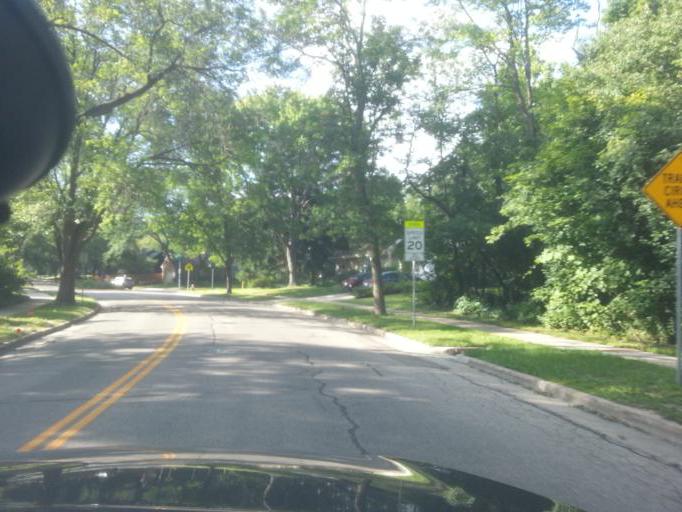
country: US
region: Wisconsin
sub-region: Dane County
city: Middleton
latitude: 43.0695
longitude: -89.4933
